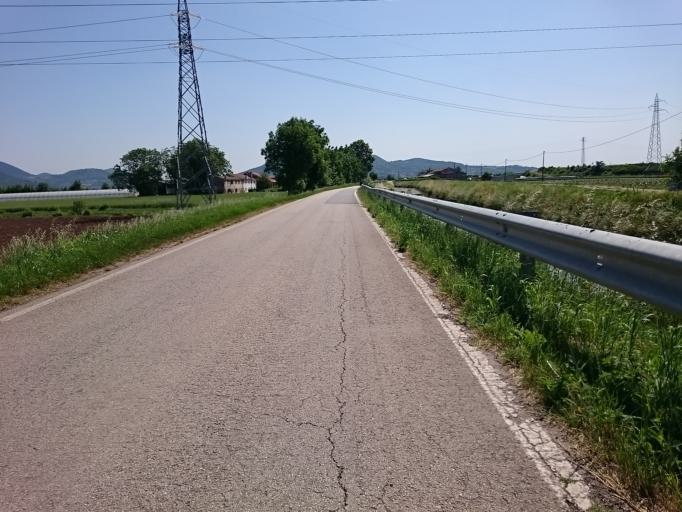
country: IT
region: Veneto
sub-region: Provincia di Padova
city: Lozzo Atestino
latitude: 45.2596
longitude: 11.5954
